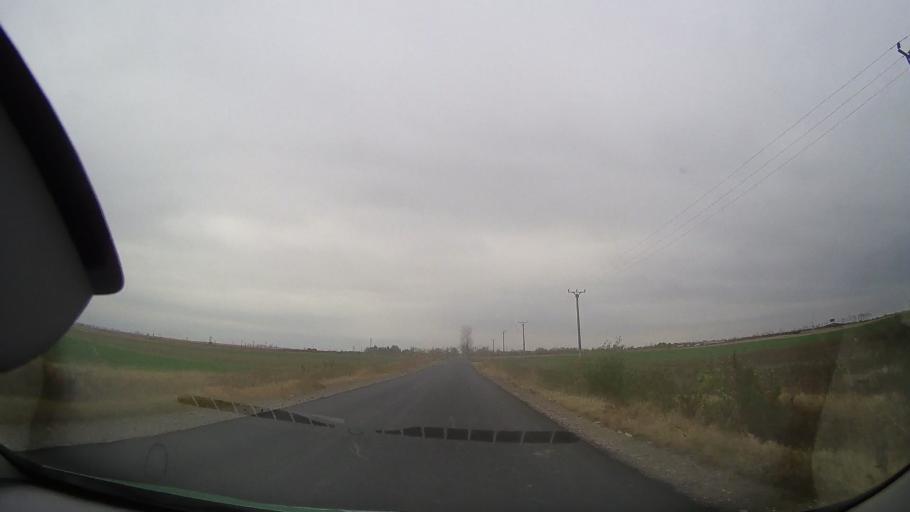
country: RO
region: Braila
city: Dudesti
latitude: 44.9416
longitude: 27.4061
